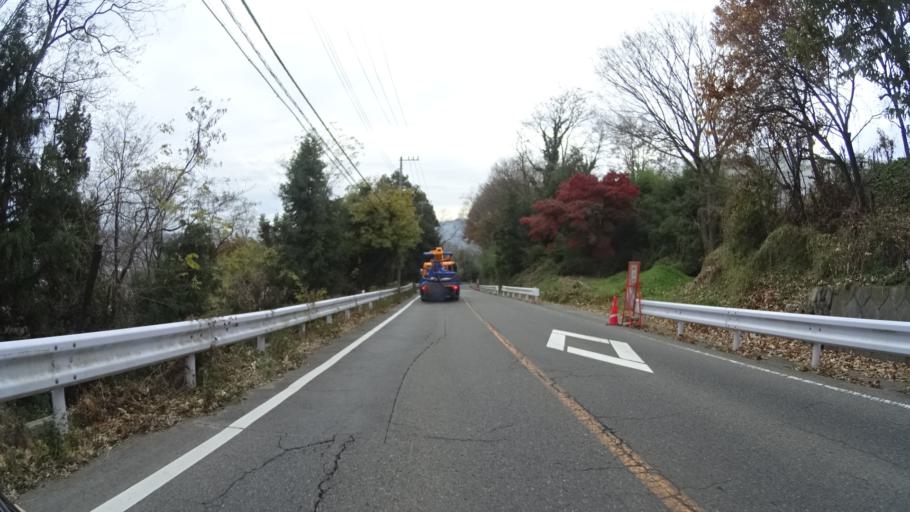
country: JP
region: Gunma
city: Numata
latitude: 36.6302
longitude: 139.0465
